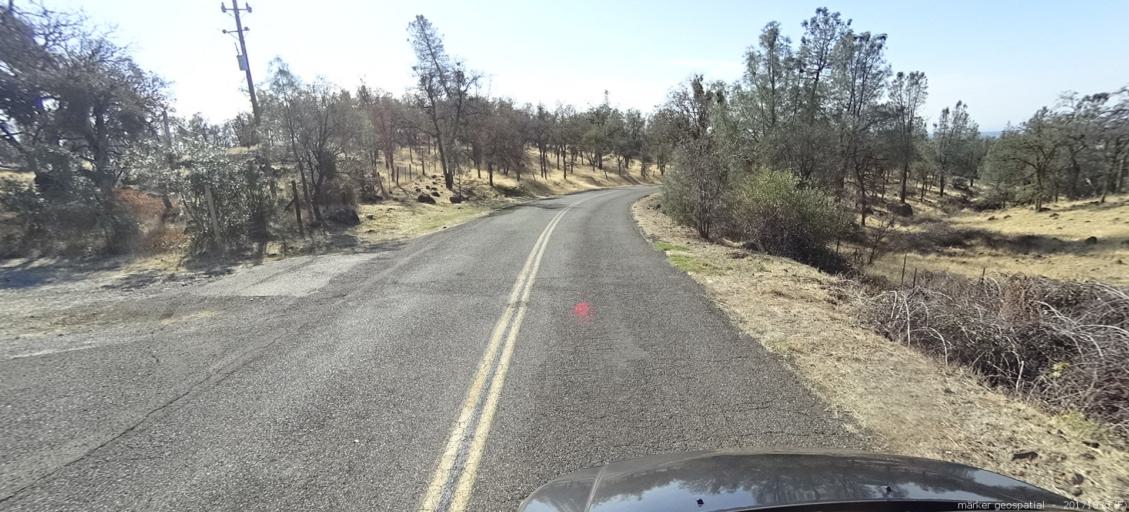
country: US
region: California
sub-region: Shasta County
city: Shingletown
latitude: 40.6620
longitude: -121.9488
